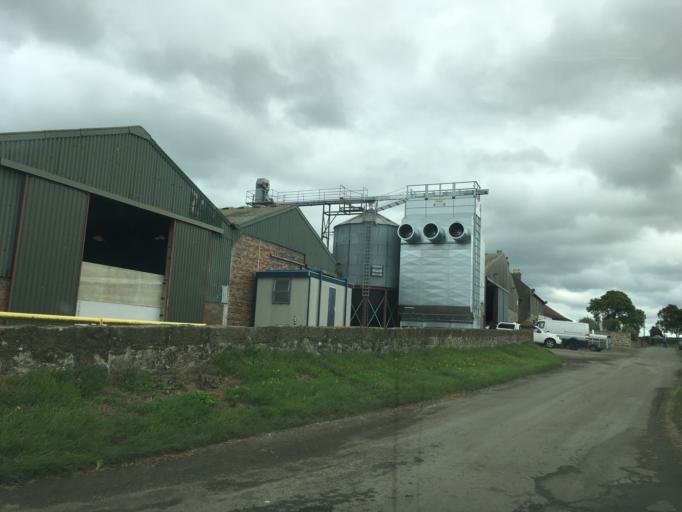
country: GB
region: Scotland
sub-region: Falkirk
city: Bo'ness
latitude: 55.9962
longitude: -3.6462
